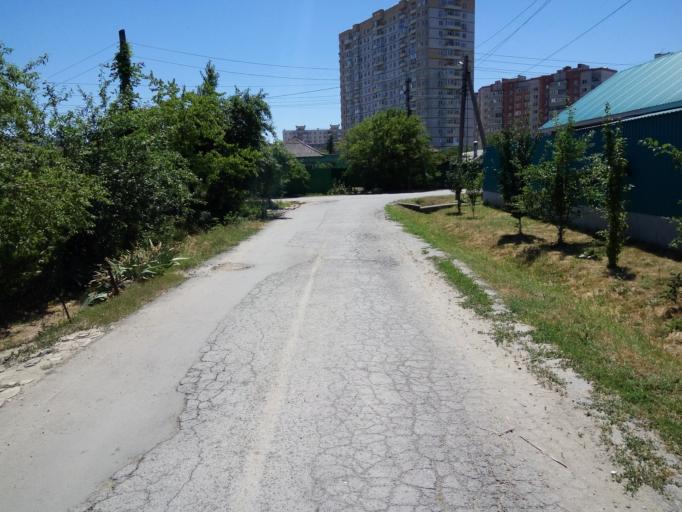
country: RU
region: Rostov
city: Bataysk
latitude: 47.1393
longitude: 39.7711
